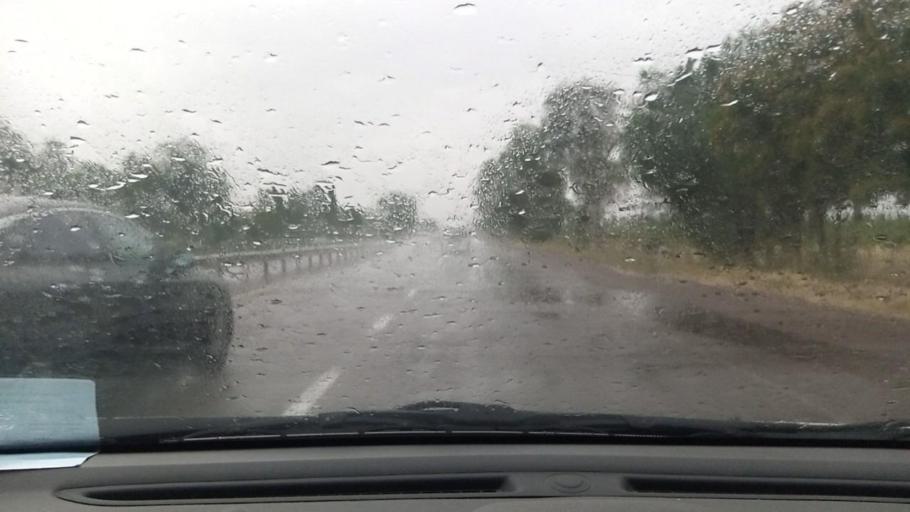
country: UZ
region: Toshkent
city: Ohangaron
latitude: 40.9368
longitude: 69.5867
